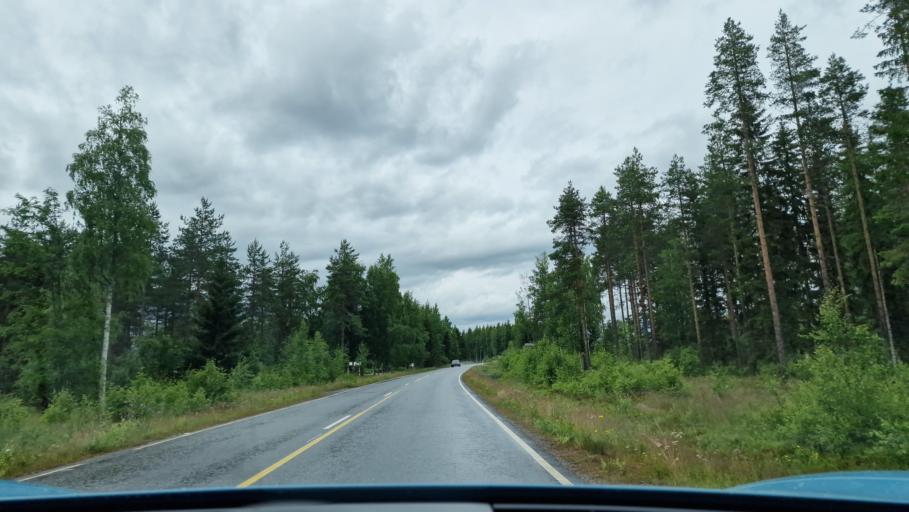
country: FI
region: Central Finland
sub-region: Saarijaervi-Viitasaari
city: Pylkoenmaeki
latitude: 62.6772
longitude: 24.5044
